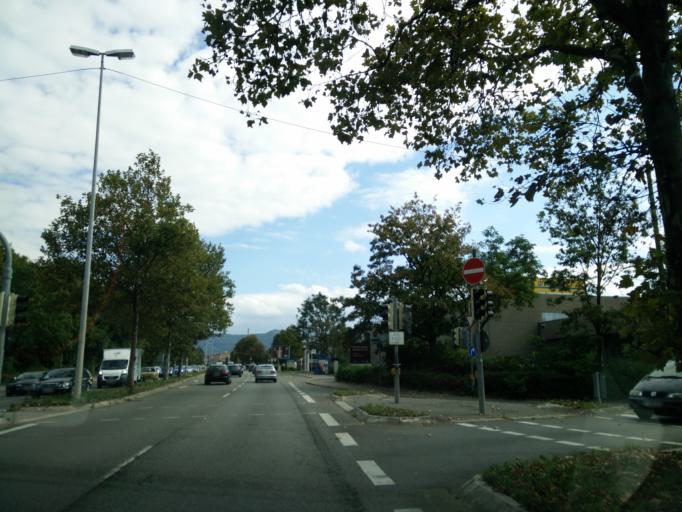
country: DE
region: Baden-Wuerttemberg
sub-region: Tuebingen Region
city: Pfullingen
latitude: 48.4843
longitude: 9.2239
